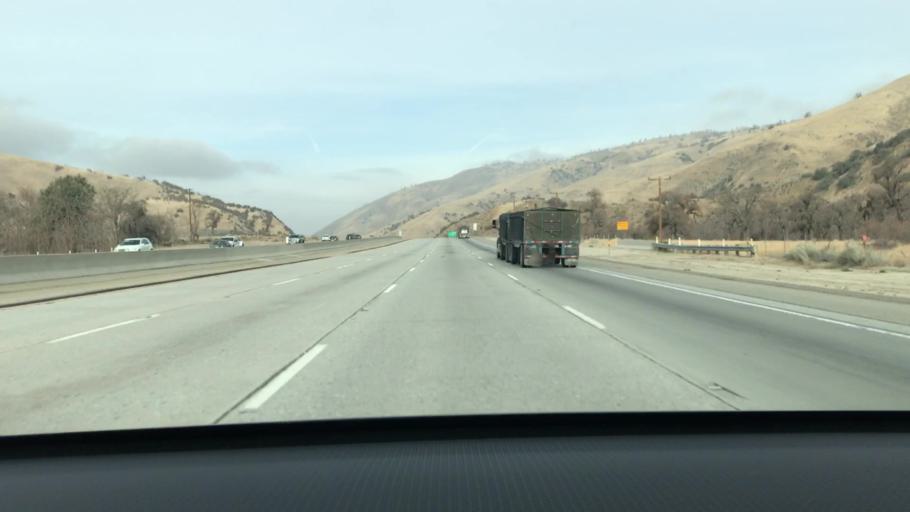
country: US
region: California
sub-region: Kern County
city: Lebec
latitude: 34.8589
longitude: -118.8769
